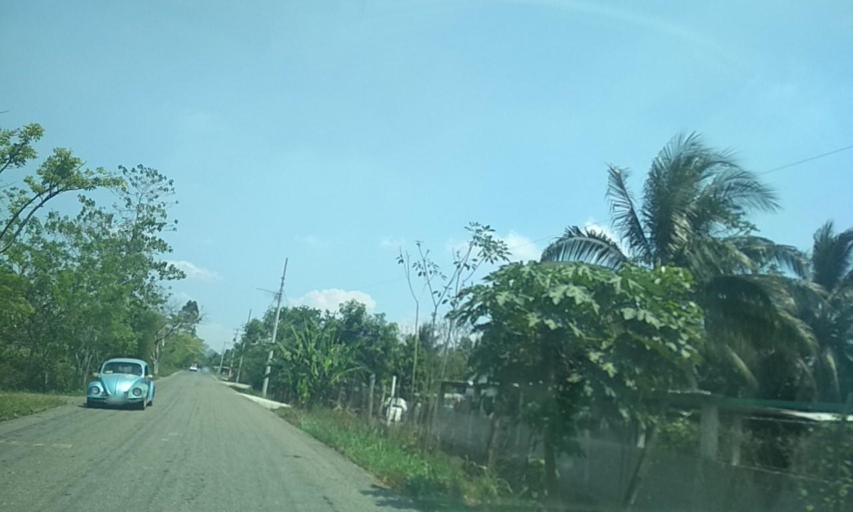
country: MX
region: Tabasco
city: Huimanguillo
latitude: 17.8045
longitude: -93.4927
